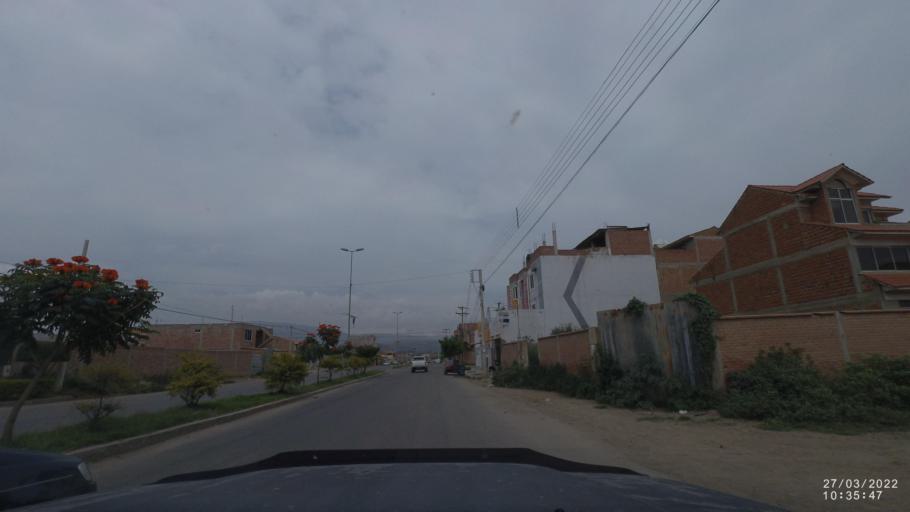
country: BO
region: Cochabamba
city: Cochabamba
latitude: -17.4402
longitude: -66.1501
